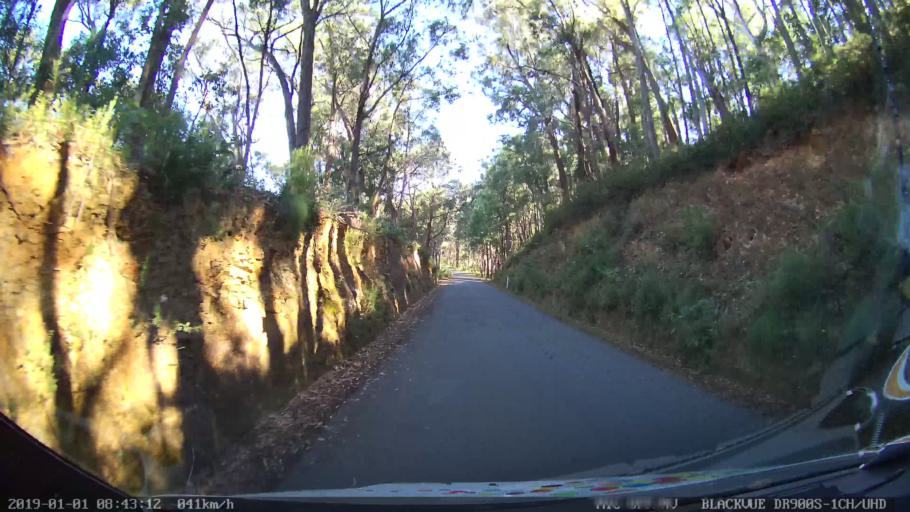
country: AU
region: New South Wales
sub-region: Snowy River
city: Jindabyne
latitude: -36.3191
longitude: 148.1934
